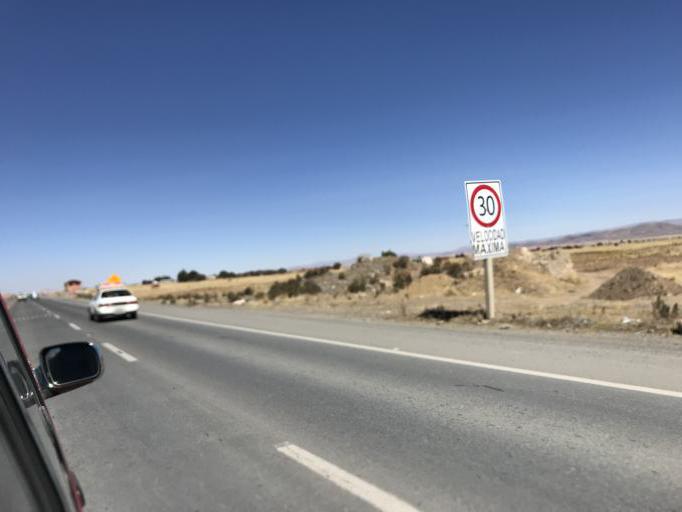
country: BO
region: La Paz
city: Batallas
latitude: -16.3436
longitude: -68.4082
